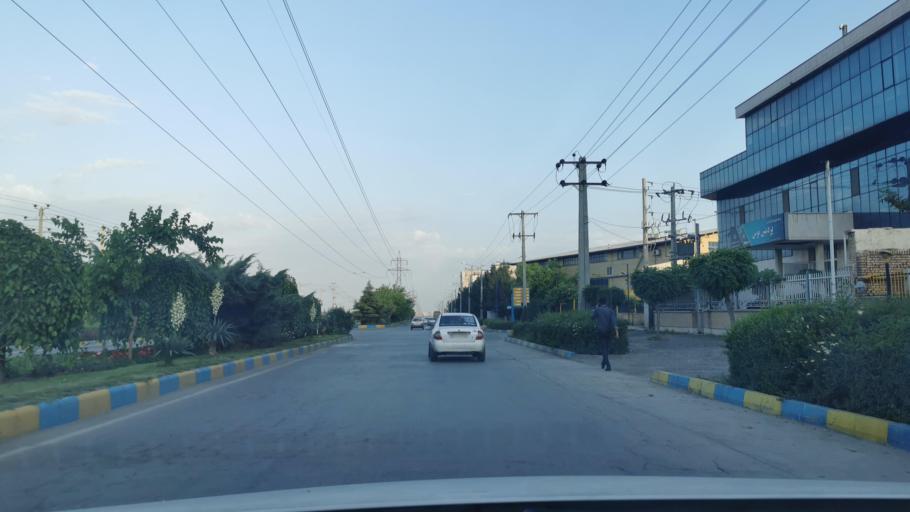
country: IR
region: Razavi Khorasan
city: Torqabeh
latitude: 36.4246
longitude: 59.4242
